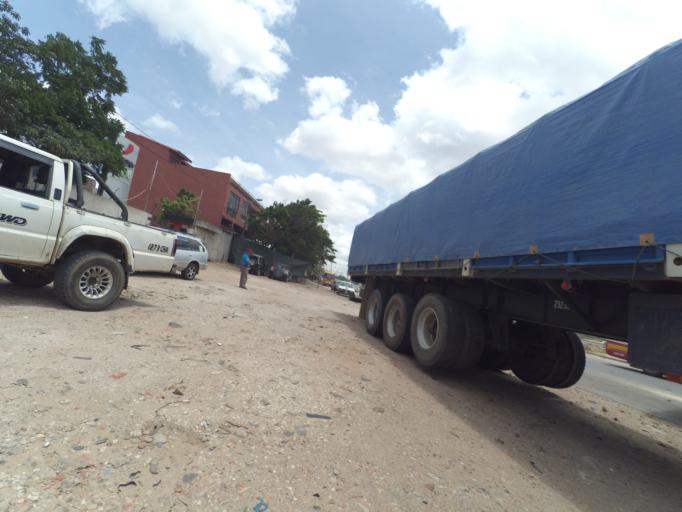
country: BO
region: Santa Cruz
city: Santa Cruz de la Sierra
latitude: -17.8146
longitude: -63.2145
